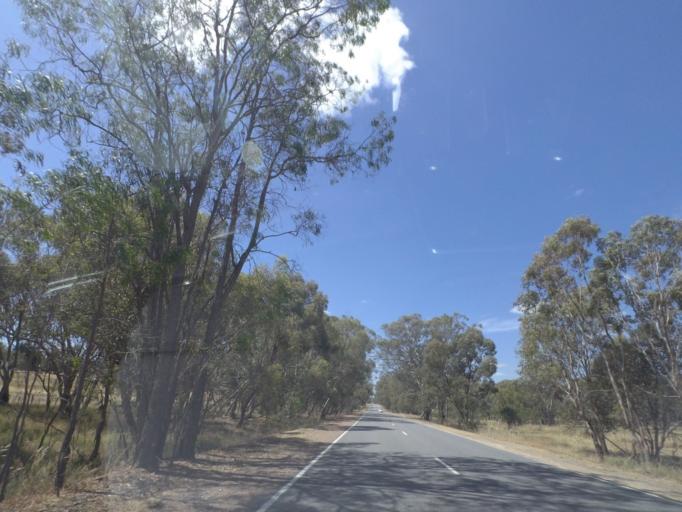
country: AU
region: Victoria
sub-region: Wangaratta
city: Wangaratta
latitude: -36.4470
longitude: 146.2409
